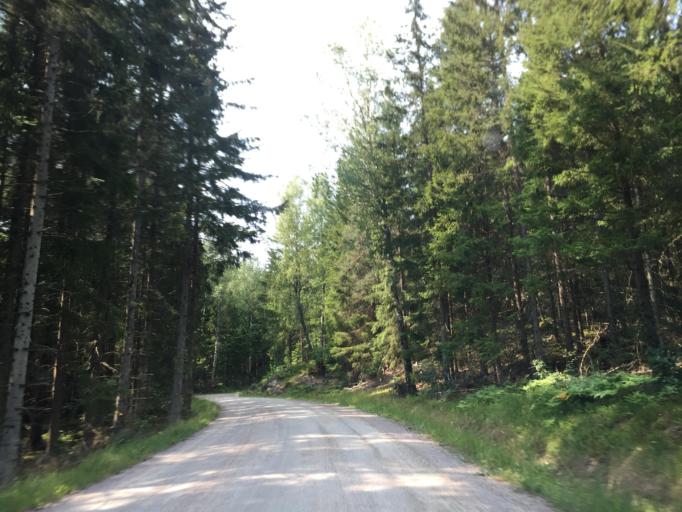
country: SE
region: Vaestra Goetaland
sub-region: Lilla Edets Kommun
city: Lilla Edet
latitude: 58.2287
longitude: 12.1179
